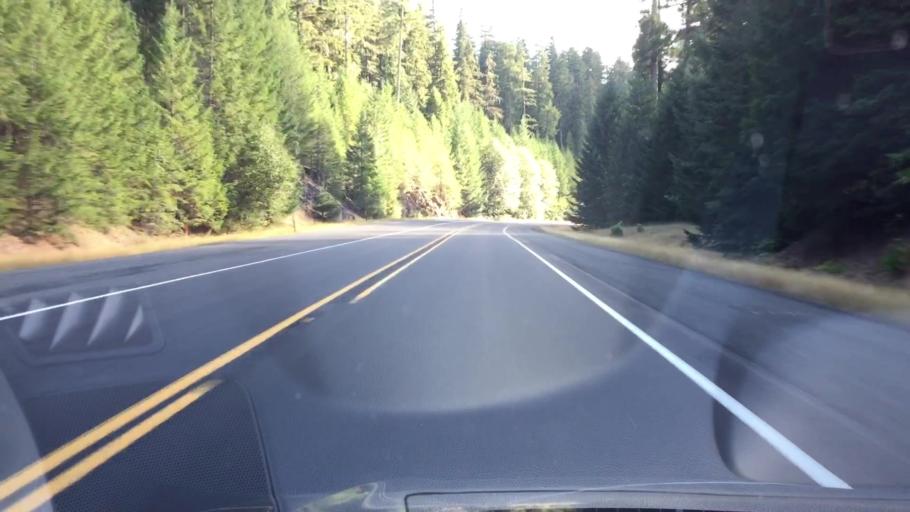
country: US
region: Washington
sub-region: Pierce County
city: Buckley
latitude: 46.6765
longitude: -121.5766
